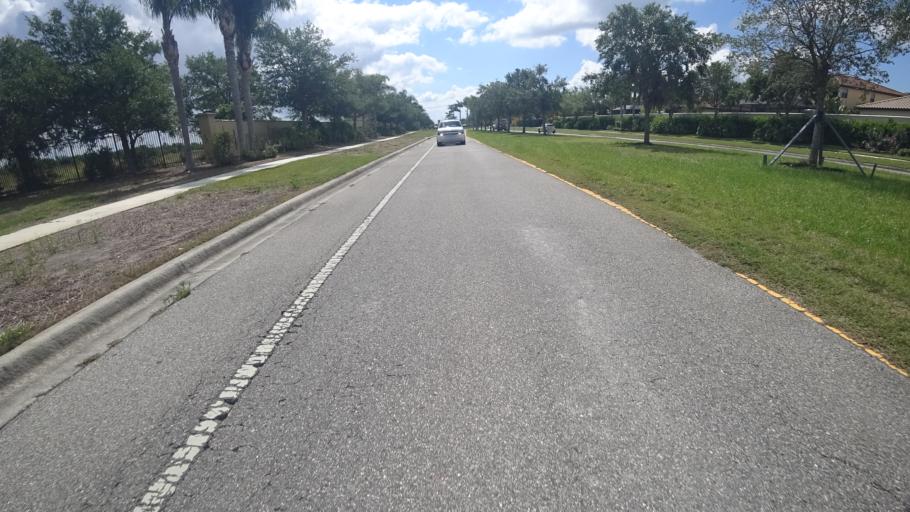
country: US
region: Florida
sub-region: Manatee County
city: Bayshore Gardens
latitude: 27.4326
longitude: -82.6186
